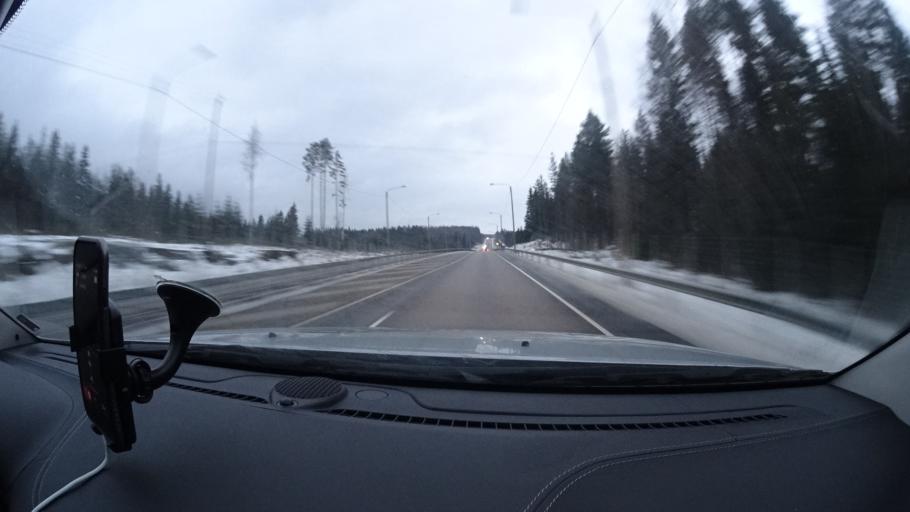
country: FI
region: Central Finland
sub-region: Jyvaeskylae
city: Toivakka
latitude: 62.0243
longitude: 26.0475
